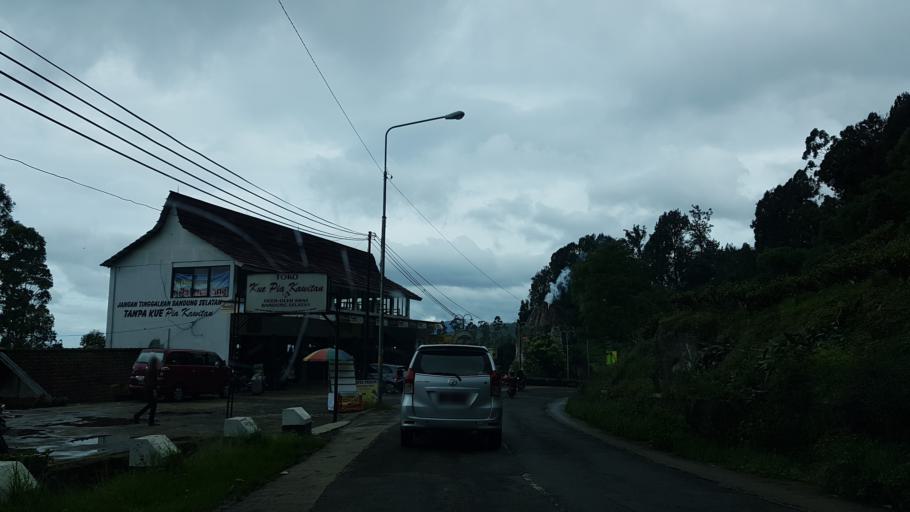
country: ID
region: West Java
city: Banjar
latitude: -7.1350
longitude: 107.4141
